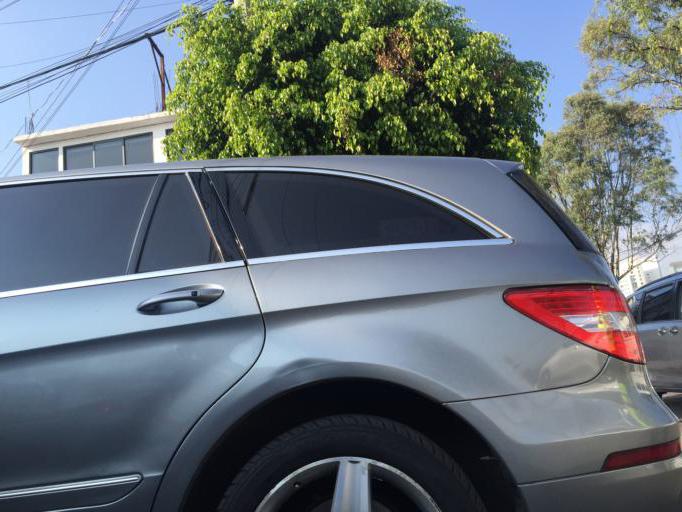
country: MX
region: Mexico City
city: Col. Bosques de las Lomas
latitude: 19.3878
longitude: -99.2654
